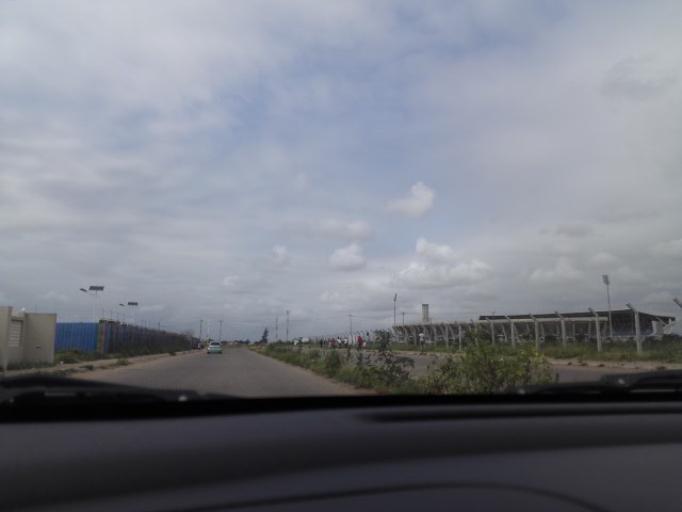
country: MZ
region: Maputo City
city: Maputo
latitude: -25.8248
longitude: 32.5804
